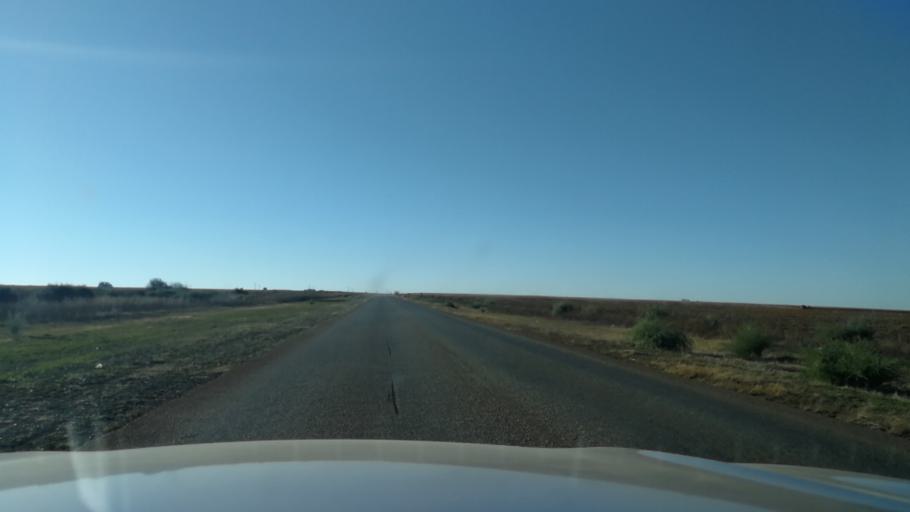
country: ZA
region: North-West
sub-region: Bojanala Platinum District Municipality
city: Rustenburg
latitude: -25.9816
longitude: 27.2638
